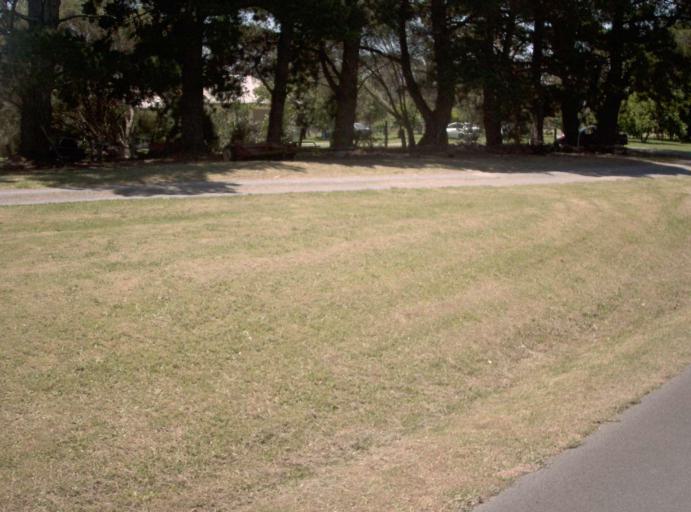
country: AU
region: Victoria
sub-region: East Gippsland
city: Lakes Entrance
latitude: -37.7570
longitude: 148.2732
